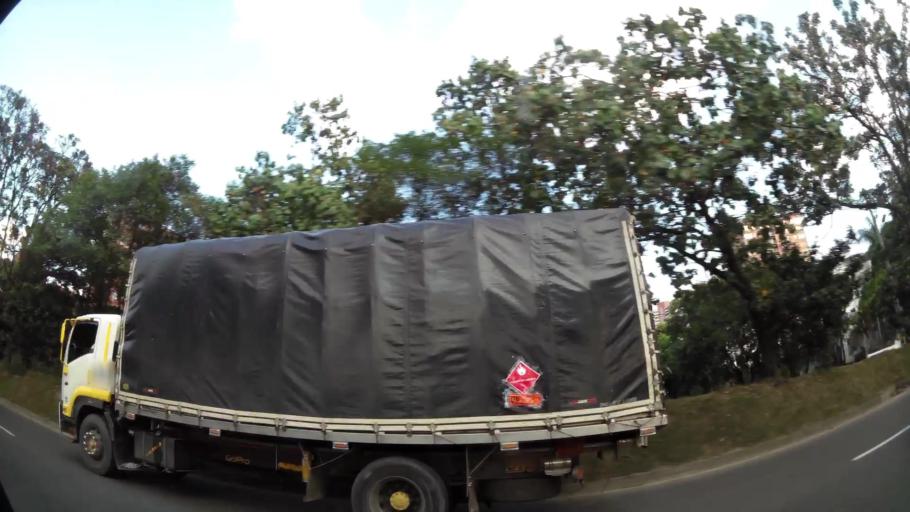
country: CO
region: Antioquia
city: Envigado
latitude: 6.1899
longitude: -75.5825
